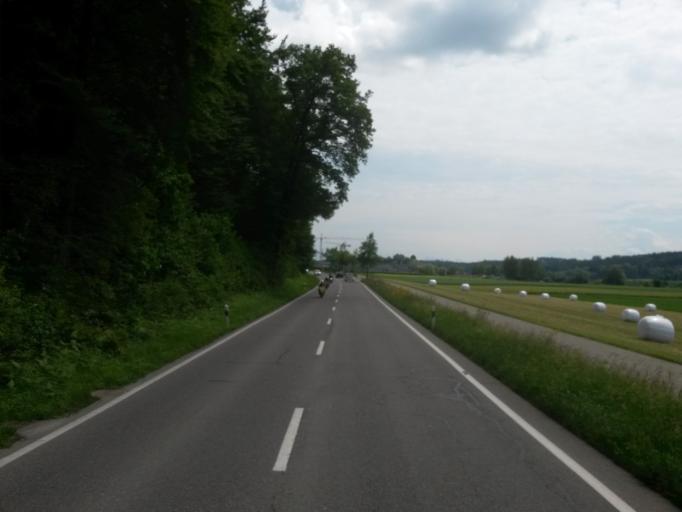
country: CH
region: Zurich
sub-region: Bezirk Pfaeffikon
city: Illnau / Unter-Illnau
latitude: 47.4002
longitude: 8.7324
